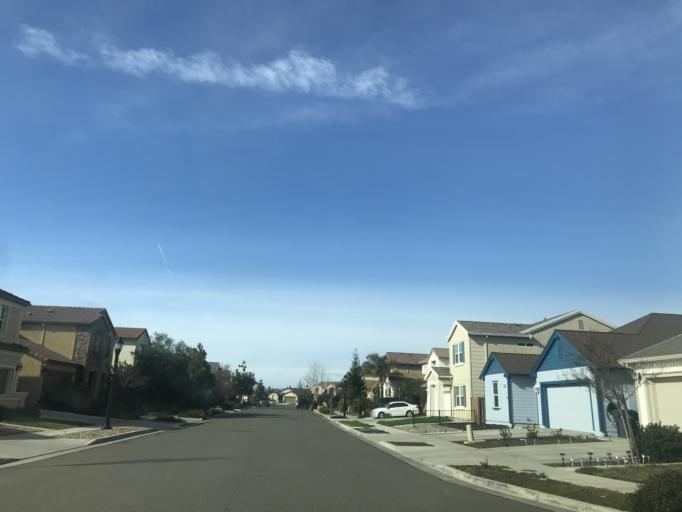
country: US
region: California
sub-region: Yolo County
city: Woodland
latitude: 38.6588
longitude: -121.7583
